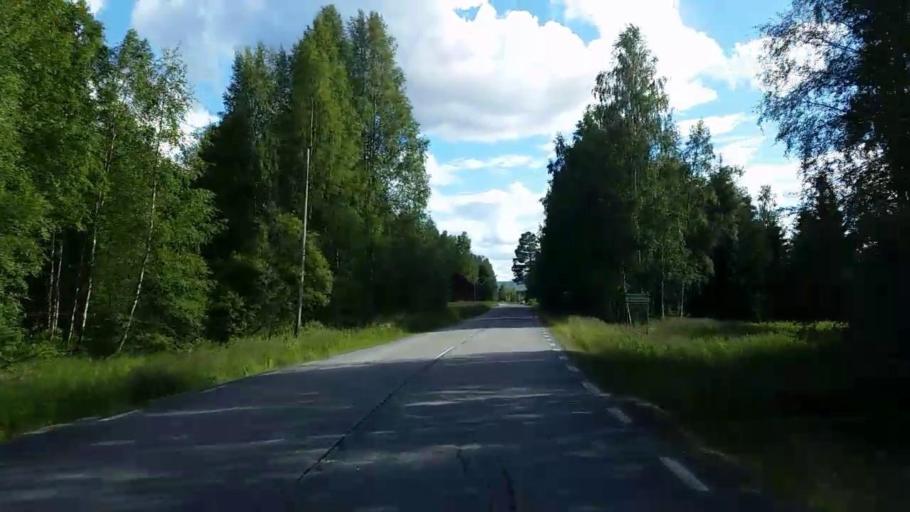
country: SE
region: Vaesternorrland
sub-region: Ange Kommun
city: Ange
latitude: 62.1649
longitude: 15.6790
